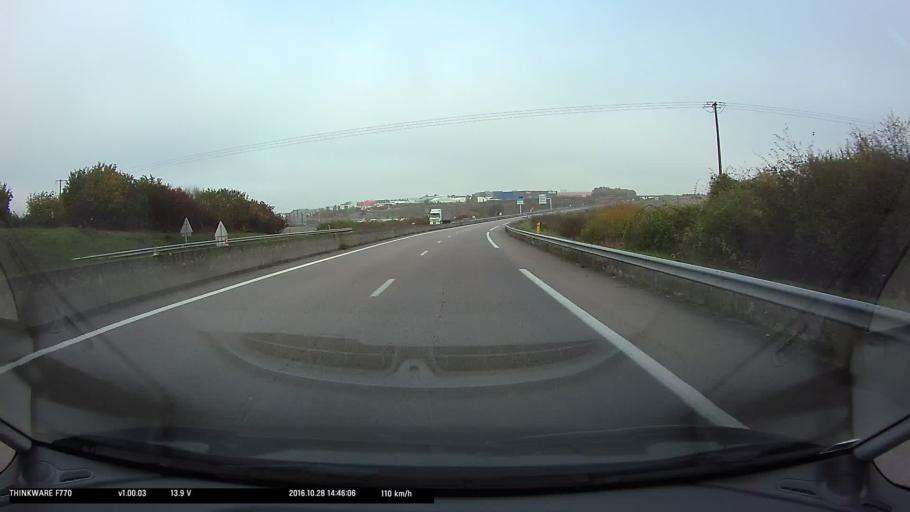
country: FR
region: Lorraine
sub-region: Departement de la Moselle
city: Sarrebourg
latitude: 48.7134
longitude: 7.0396
